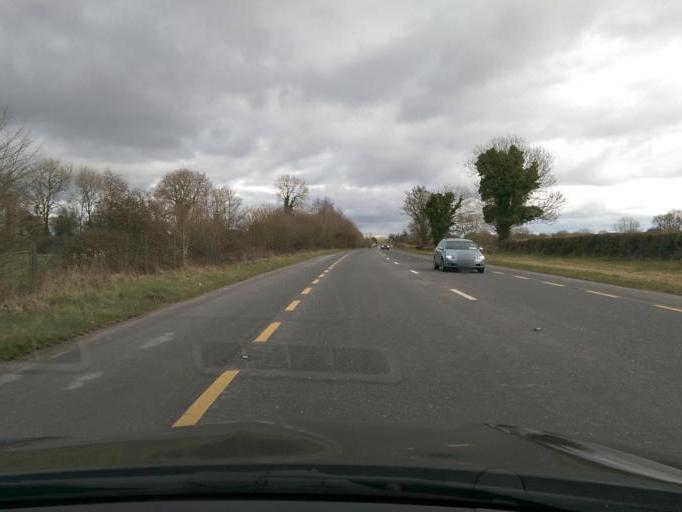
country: IE
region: Leinster
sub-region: An Iarmhi
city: Moate
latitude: 53.3916
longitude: -7.7953
